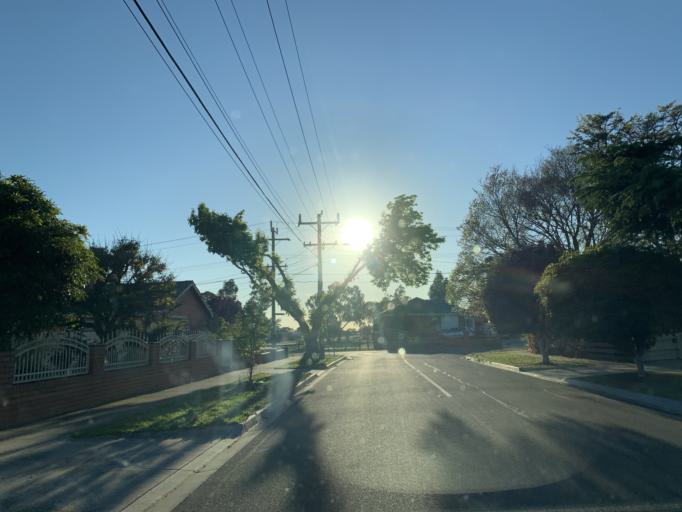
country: AU
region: Victoria
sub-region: Brimbank
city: St Albans
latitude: -37.7498
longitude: 144.8080
